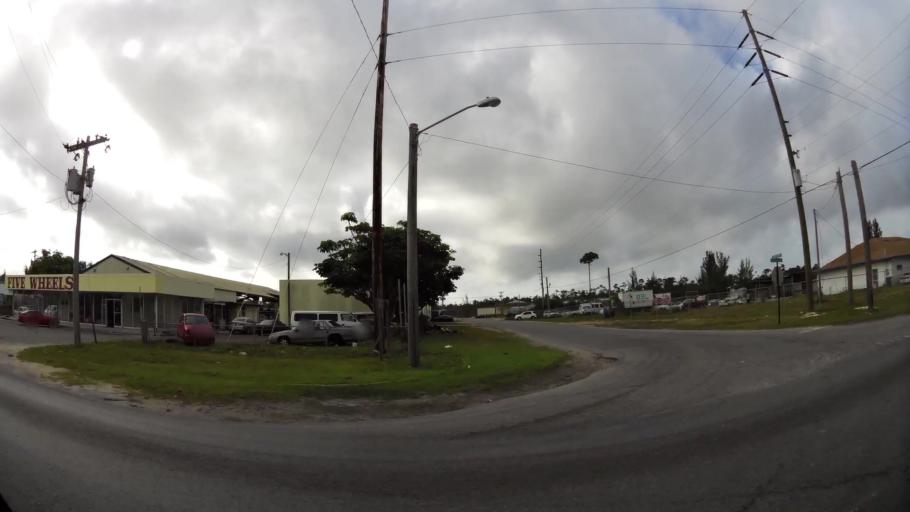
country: BS
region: Freeport
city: Freeport
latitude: 26.5374
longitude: -78.7139
